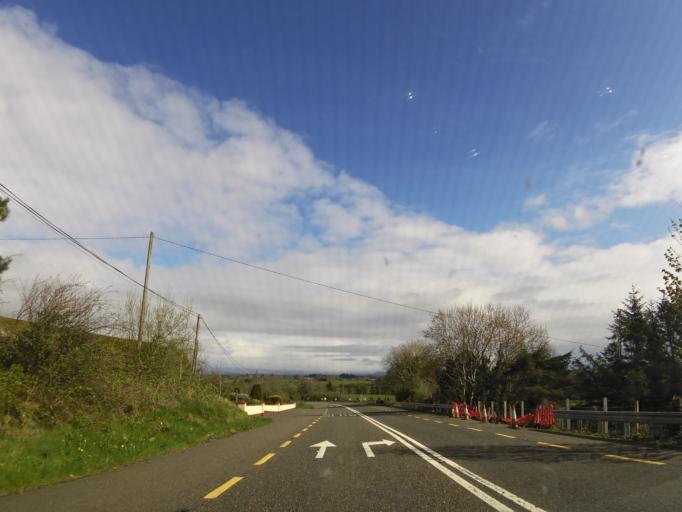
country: IE
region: Connaught
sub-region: Sligo
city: Tobercurry
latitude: 53.9245
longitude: -8.7842
